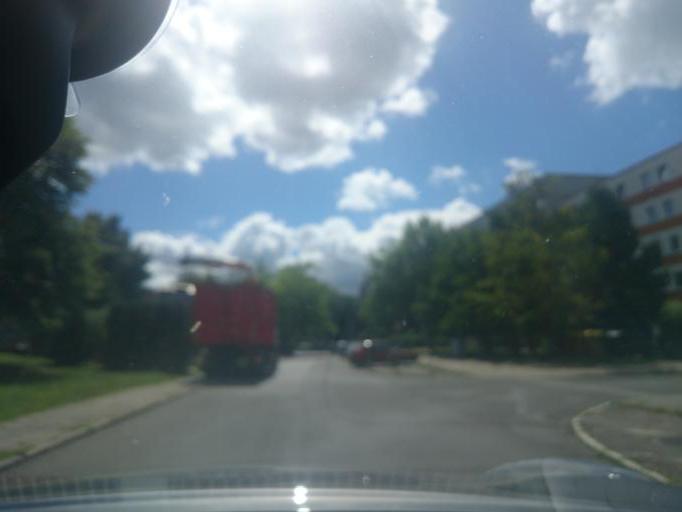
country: DE
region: Mecklenburg-Vorpommern
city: Lambrechtshagen
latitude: 54.1205
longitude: 12.0553
